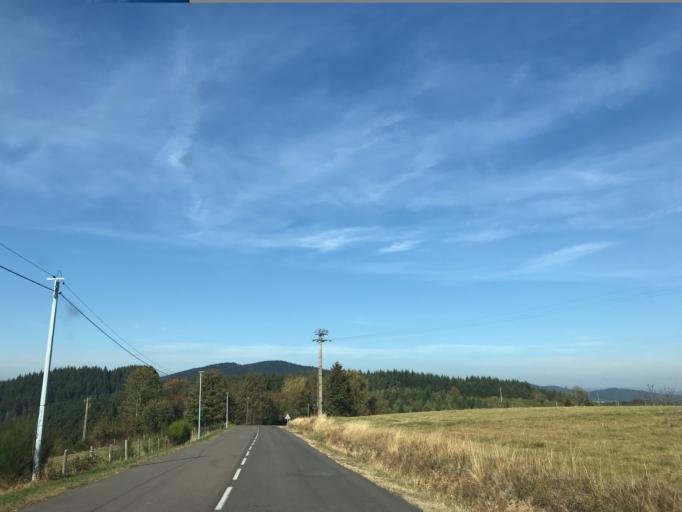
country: FR
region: Rhone-Alpes
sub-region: Departement de la Loire
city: Noiretable
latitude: 45.8066
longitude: 3.7339
